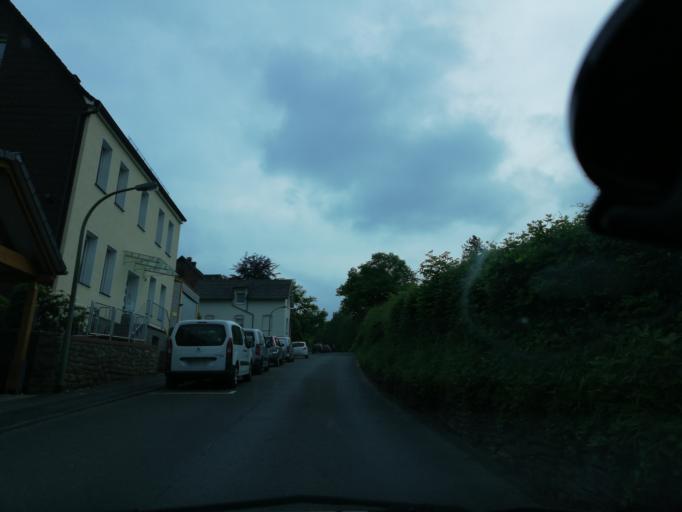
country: DE
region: North Rhine-Westphalia
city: Wetter (Ruhr)
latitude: 51.3692
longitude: 7.3811
